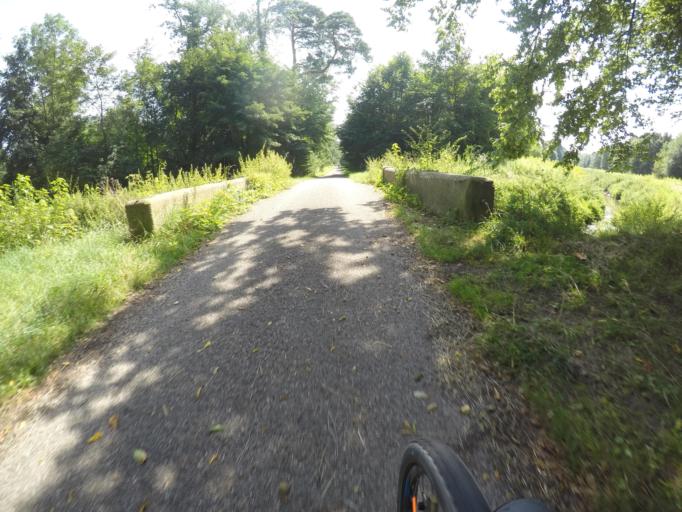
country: DE
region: Baden-Wuerttemberg
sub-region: Karlsruhe Region
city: Kronau
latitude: 49.2136
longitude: 8.5867
